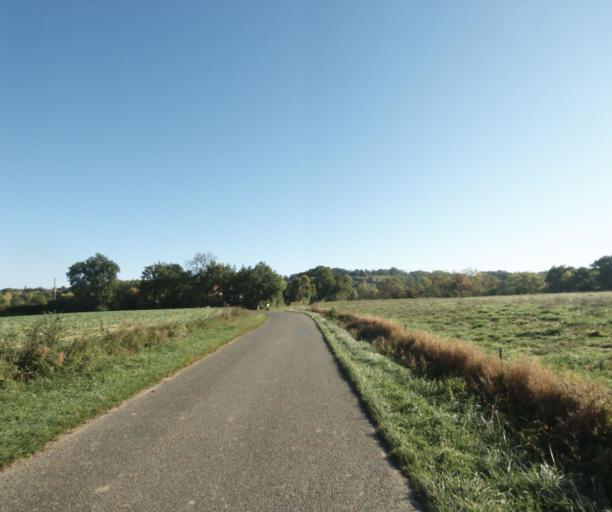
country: FR
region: Midi-Pyrenees
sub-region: Departement du Gers
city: Gondrin
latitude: 43.8417
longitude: 0.2402
